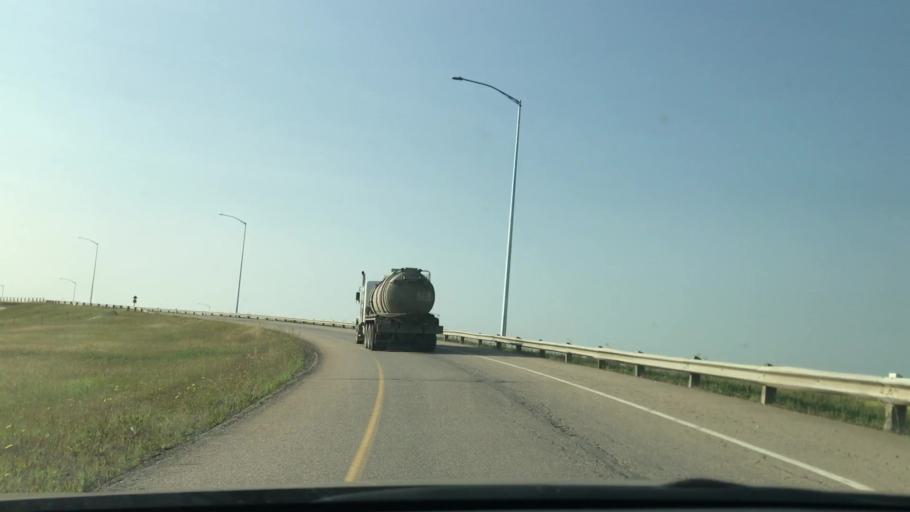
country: CA
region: Alberta
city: Leduc
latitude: 53.2862
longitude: -113.5518
